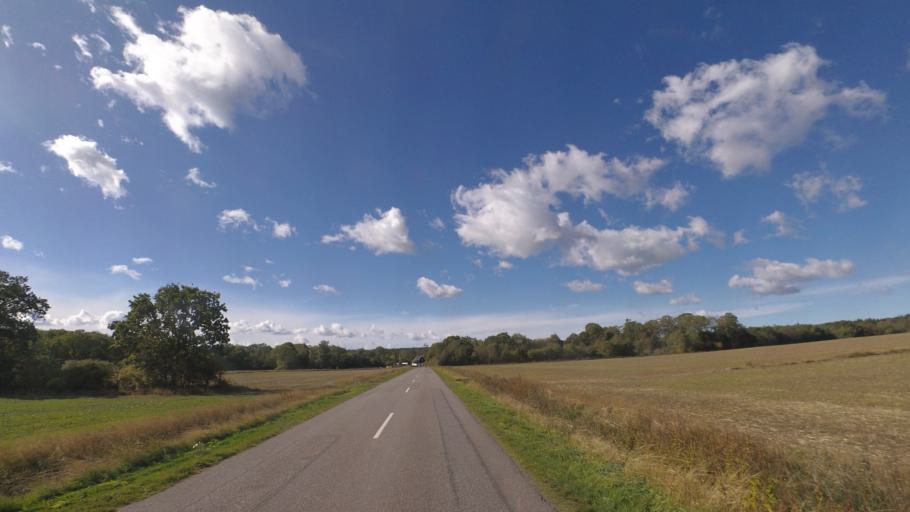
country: DK
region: Capital Region
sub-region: Bornholm Kommune
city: Nexo
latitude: 55.0777
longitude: 15.0832
